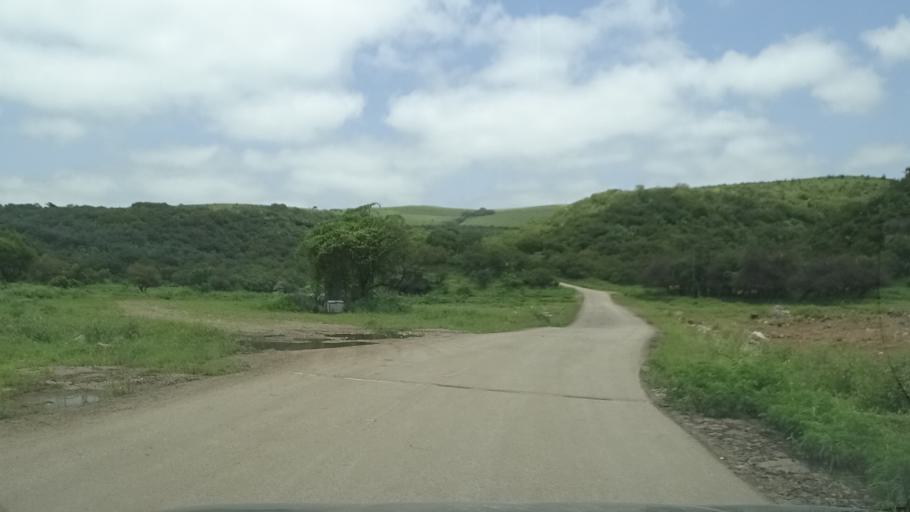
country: OM
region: Zufar
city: Salalah
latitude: 17.1978
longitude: 54.1815
